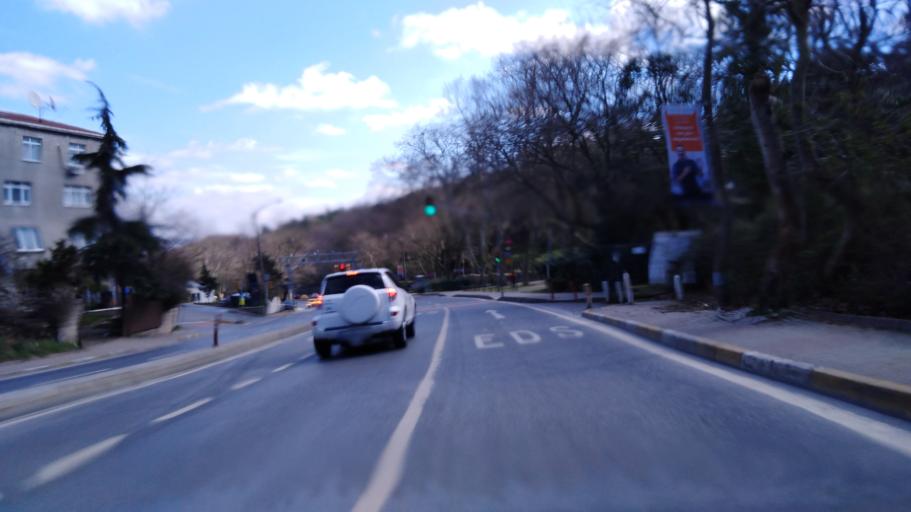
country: TR
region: Istanbul
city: Sisli
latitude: 41.1106
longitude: 29.0482
